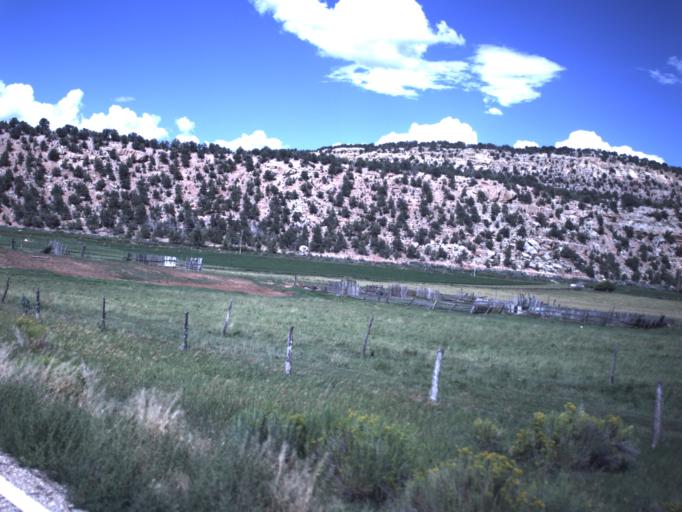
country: US
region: Utah
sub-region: Duchesne County
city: Duchesne
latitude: 40.3261
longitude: -110.6714
